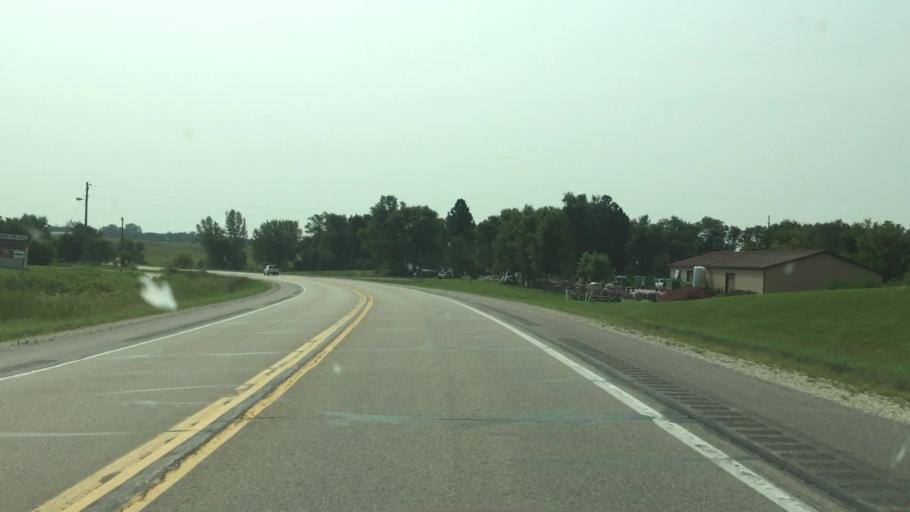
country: US
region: Iowa
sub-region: Dickinson County
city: Milford
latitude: 43.3447
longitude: -95.1789
